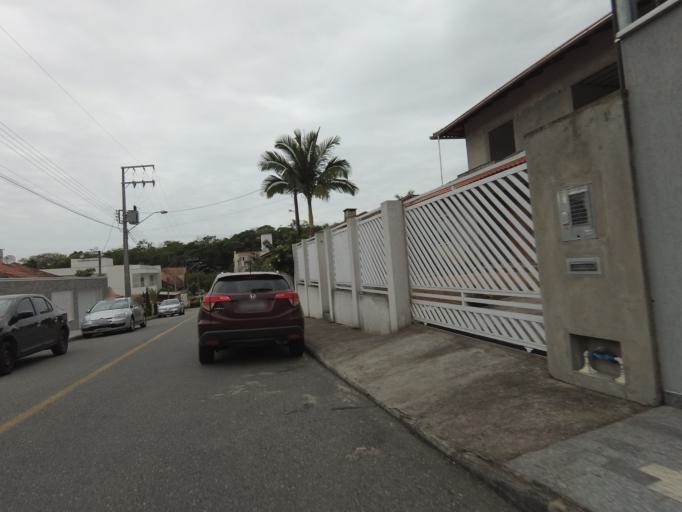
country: BR
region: Santa Catarina
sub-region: Blumenau
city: Blumenau
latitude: -26.9010
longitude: -49.1314
